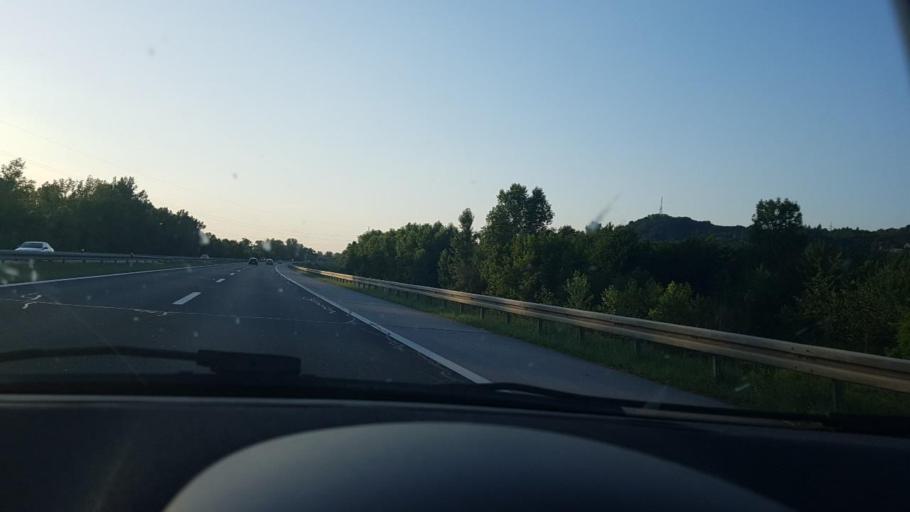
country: HR
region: Zagrebacka
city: Bestovje
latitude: 45.8164
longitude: 15.8253
